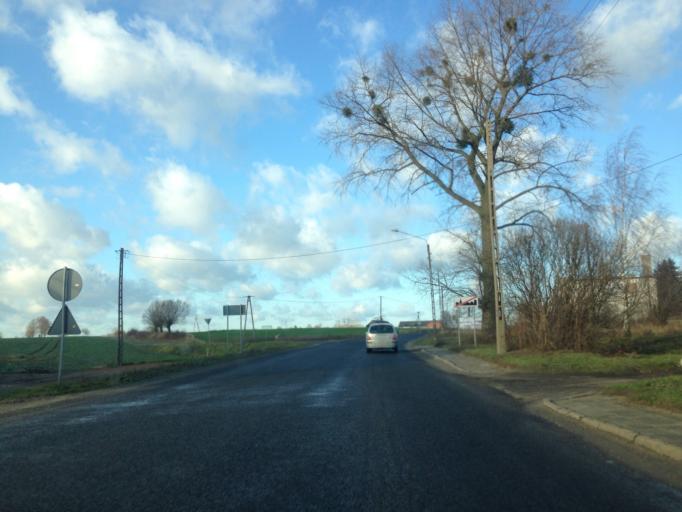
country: PL
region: Kujawsko-Pomorskie
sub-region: Powiat grudziadzki
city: Lasin
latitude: 53.5285
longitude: 19.0739
